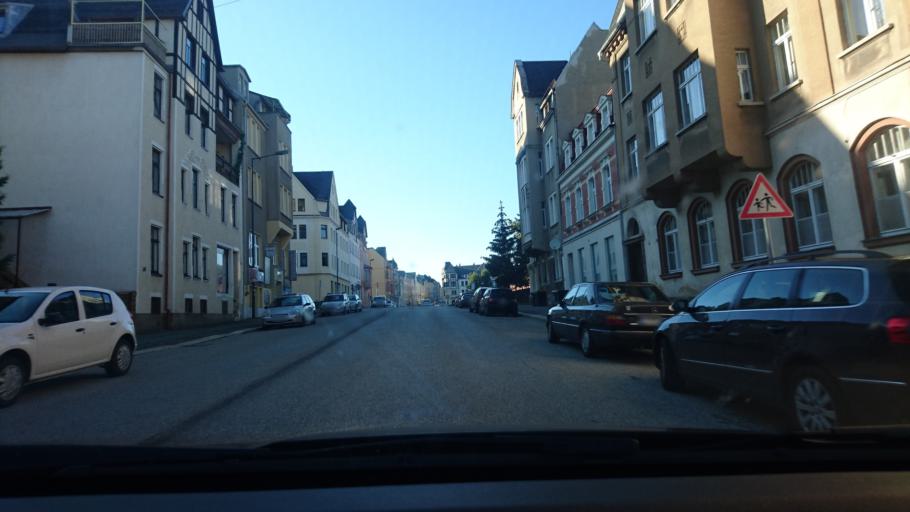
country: DE
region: Saxony
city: Auerbach
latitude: 50.5050
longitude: 12.3958
